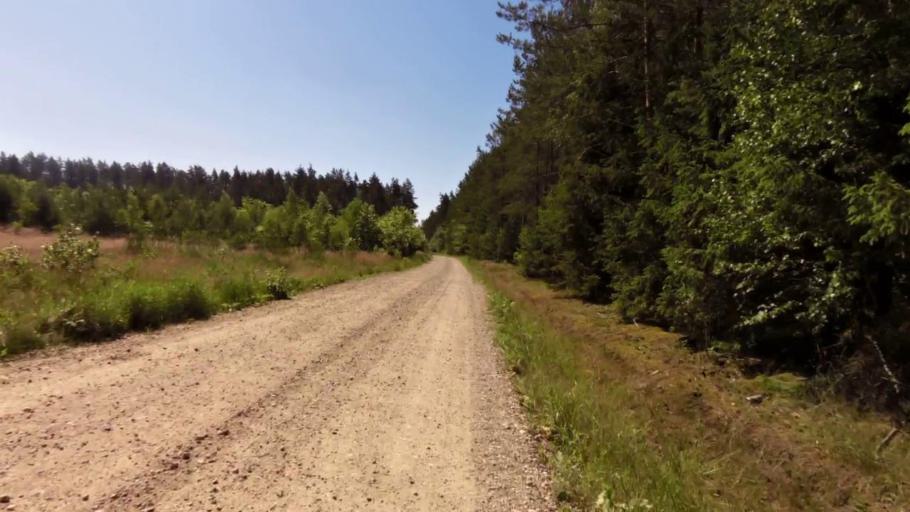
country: PL
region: West Pomeranian Voivodeship
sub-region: Powiat swidwinski
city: Rabino
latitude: 53.9038
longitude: 16.0074
